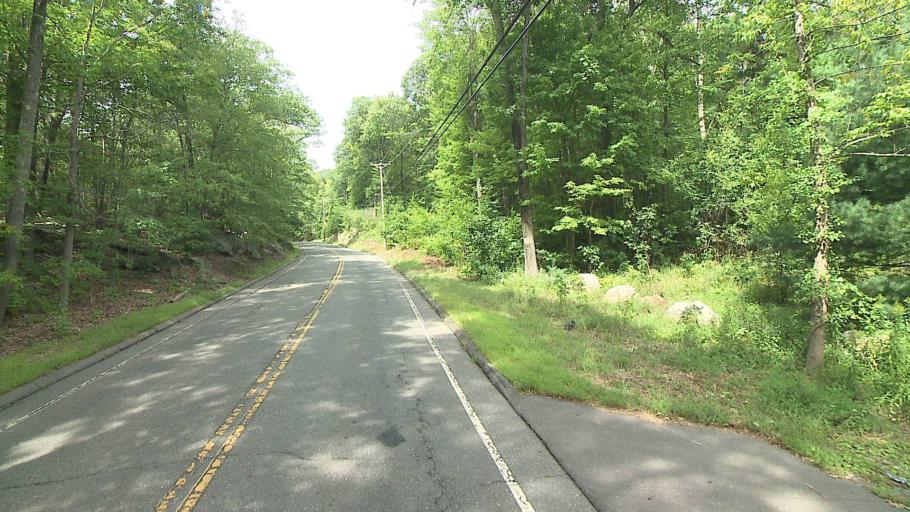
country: US
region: Connecticut
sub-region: Litchfield County
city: Oakville
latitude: 41.6229
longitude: -73.0489
